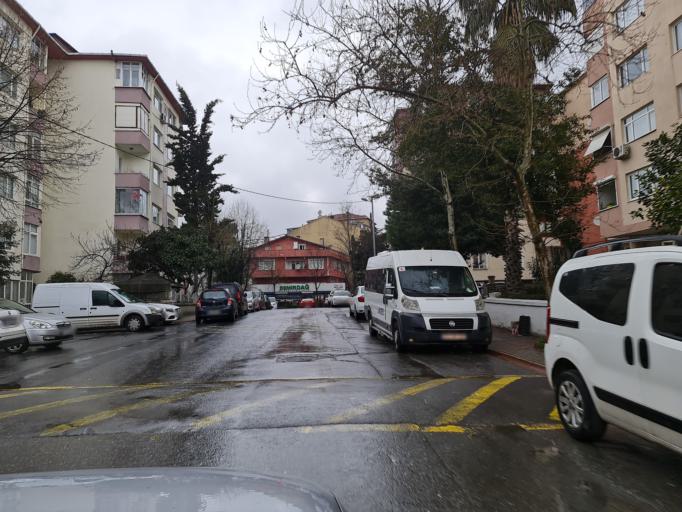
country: TR
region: Istanbul
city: Umraniye
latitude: 41.0107
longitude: 29.1016
